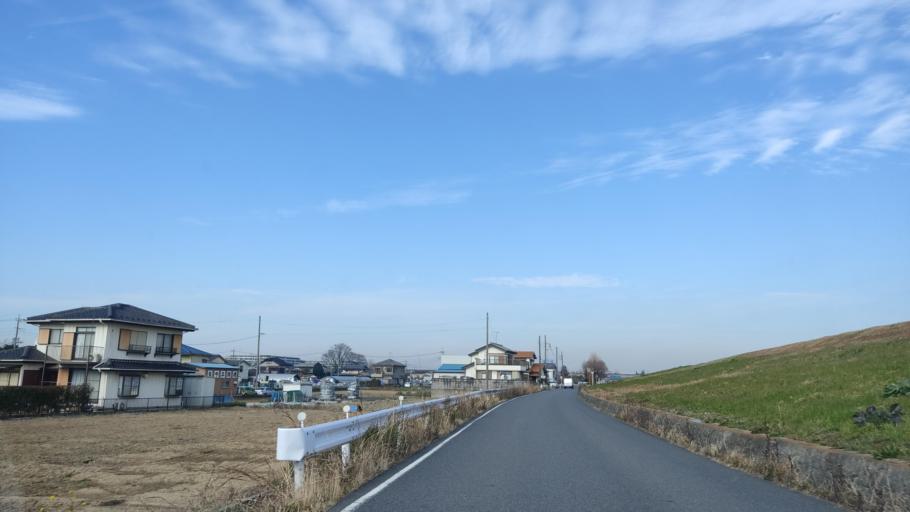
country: JP
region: Chiba
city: Nagareyama
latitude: 35.8251
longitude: 139.8856
